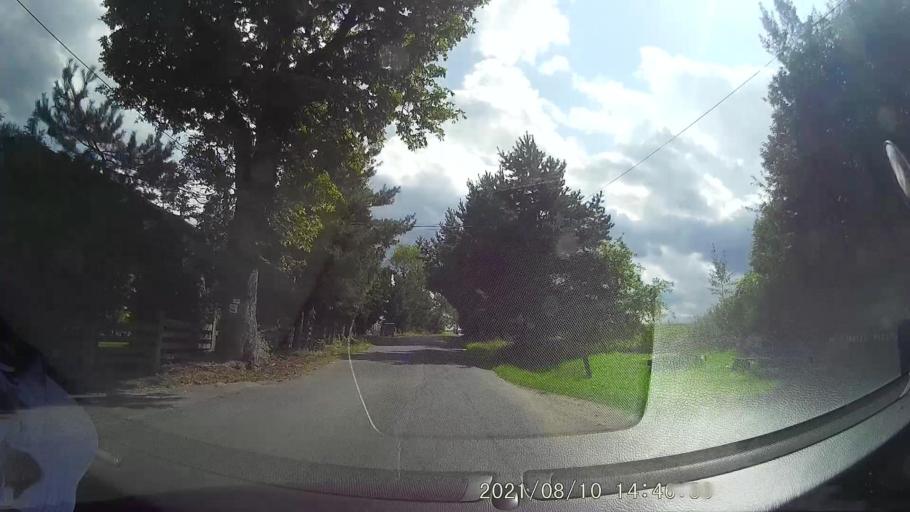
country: PL
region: Lower Silesian Voivodeship
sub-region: Powiat klodzki
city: Radkow
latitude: 50.5287
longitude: 16.4126
